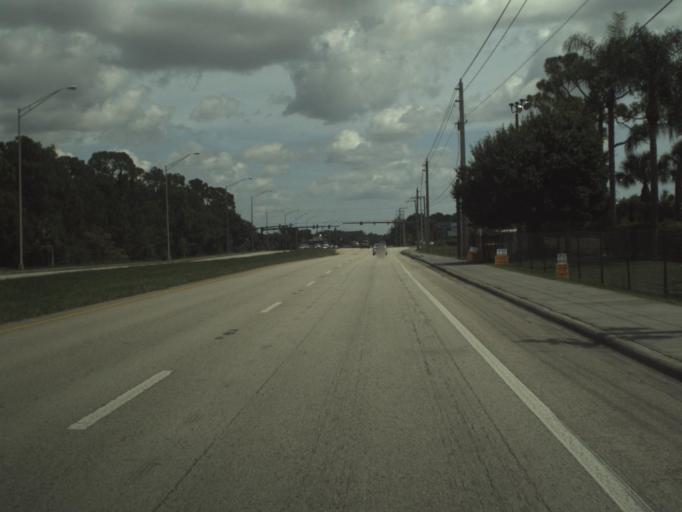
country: US
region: Florida
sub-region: Martin County
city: Palm City
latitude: 27.1215
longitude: -80.2527
